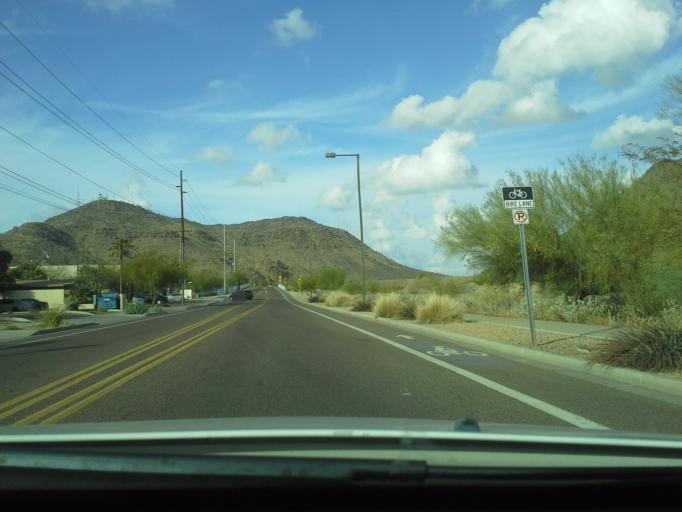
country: US
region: Arizona
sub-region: Maricopa County
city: Glendale
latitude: 33.5788
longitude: -112.0826
